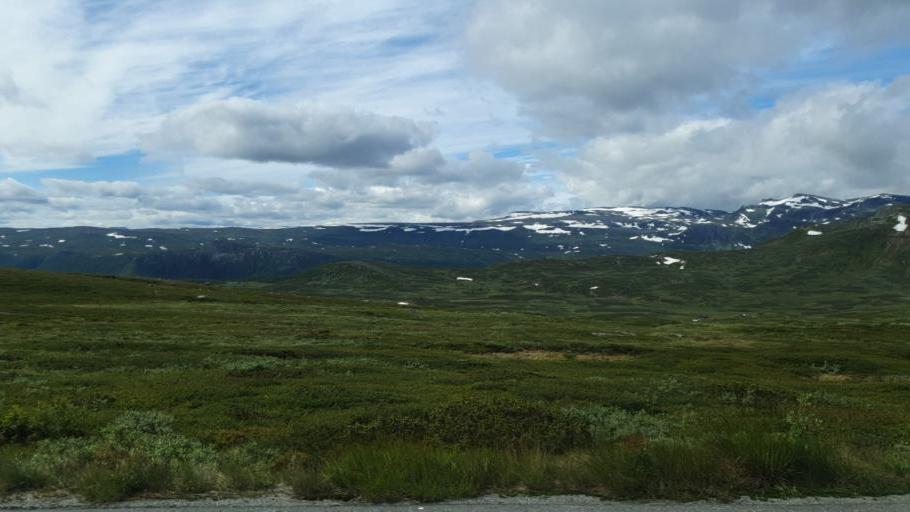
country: NO
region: Oppland
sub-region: Vestre Slidre
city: Slidre
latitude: 61.2856
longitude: 8.8269
